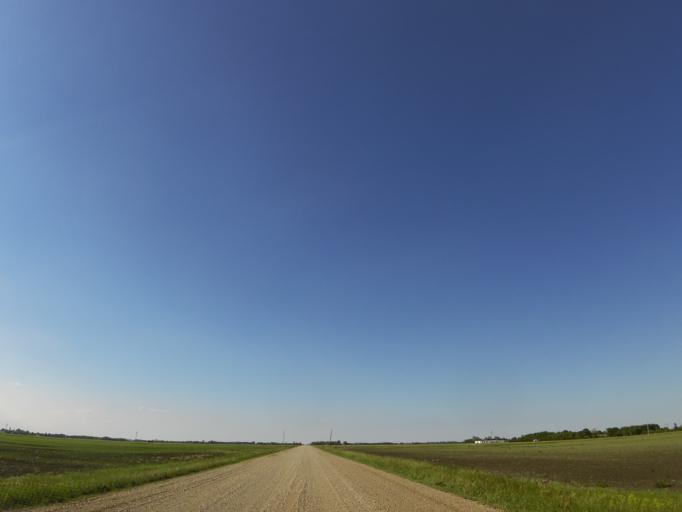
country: US
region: North Dakota
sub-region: Walsh County
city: Grafton
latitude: 48.4080
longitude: -97.2777
